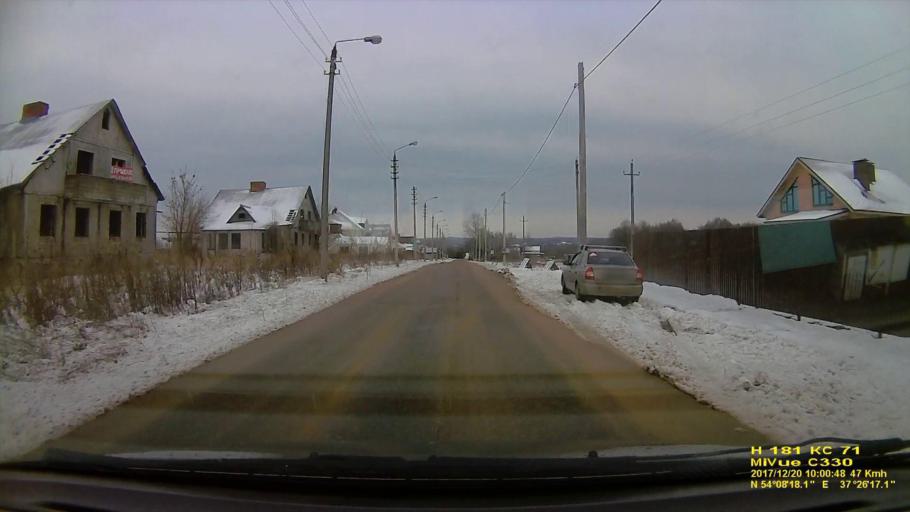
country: RU
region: Tula
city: Kosaya Gora
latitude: 54.1383
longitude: 37.4381
